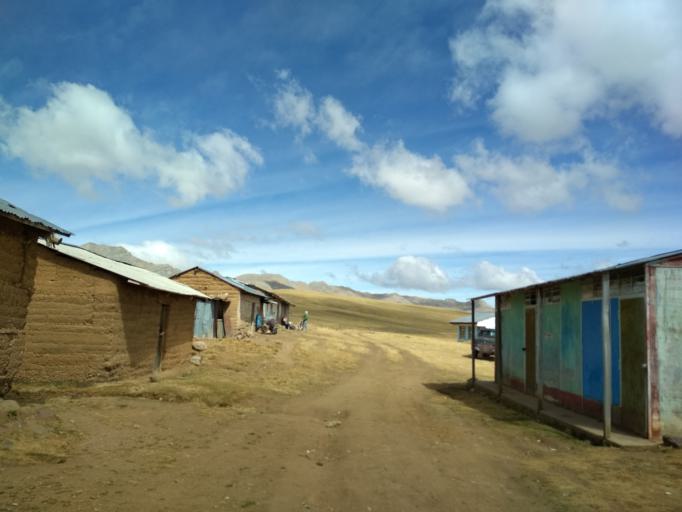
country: PE
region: Huancavelica
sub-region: Provincia de Huancavelica
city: Acobambilla
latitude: -12.7257
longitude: -75.5075
